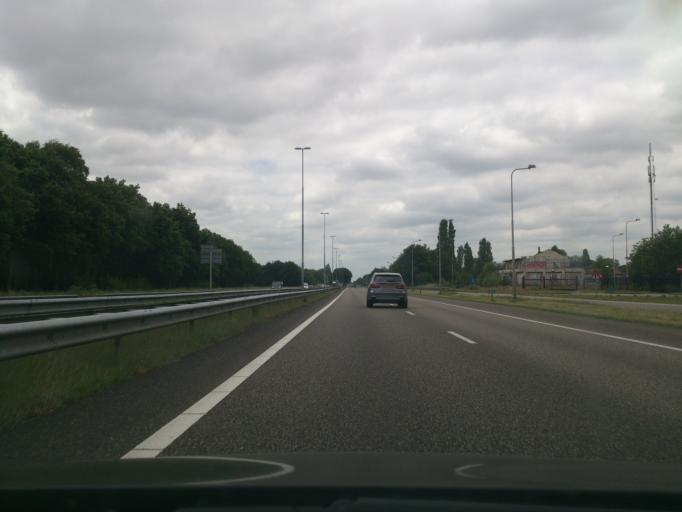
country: NL
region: North Brabant
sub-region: Gemeente Maasdonk
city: Geffen
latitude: 51.7334
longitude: 5.4907
